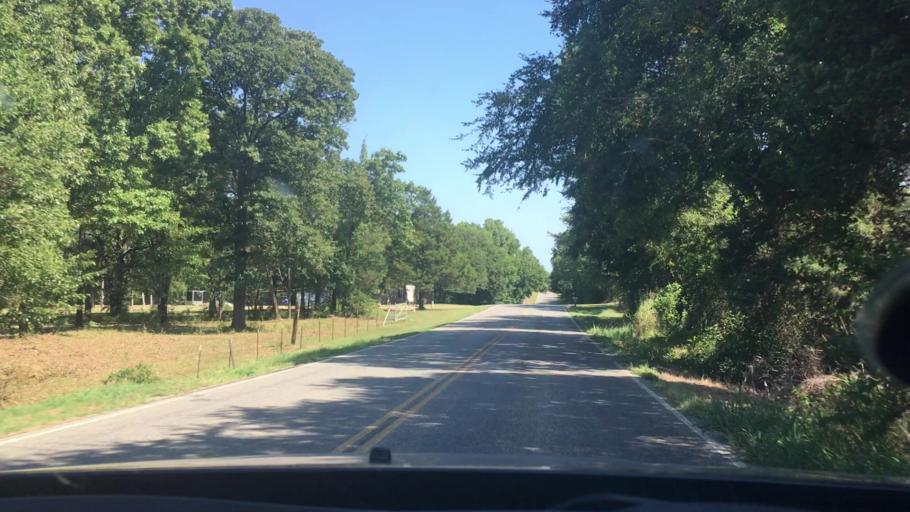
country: US
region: Oklahoma
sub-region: Johnston County
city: Tishomingo
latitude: 34.2625
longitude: -96.6186
